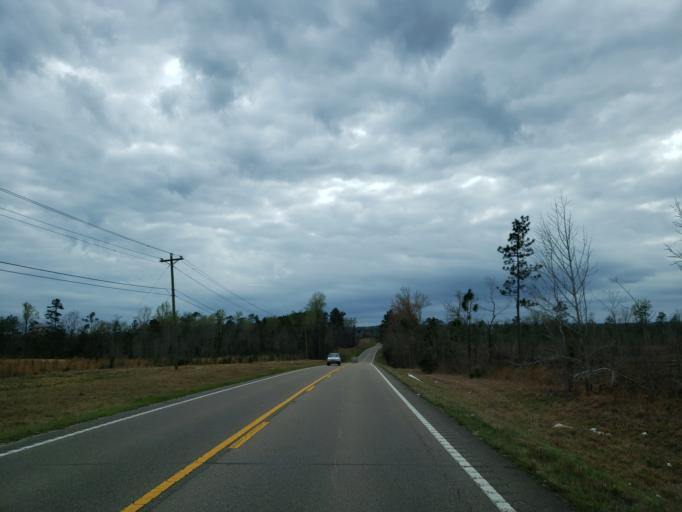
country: US
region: Mississippi
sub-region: Lamar County
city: Purvis
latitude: 31.2015
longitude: -89.3676
